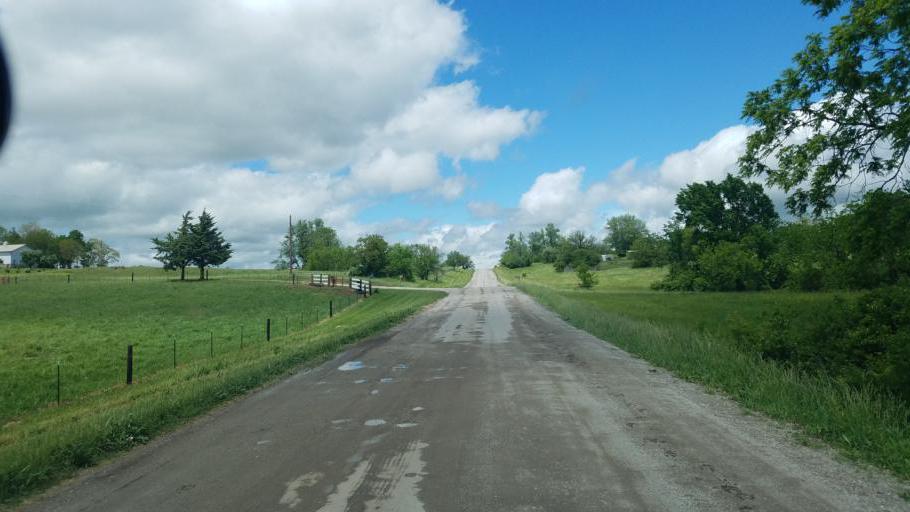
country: US
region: Iowa
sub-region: Decatur County
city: Lamoni
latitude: 40.6274
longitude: -93.8959
